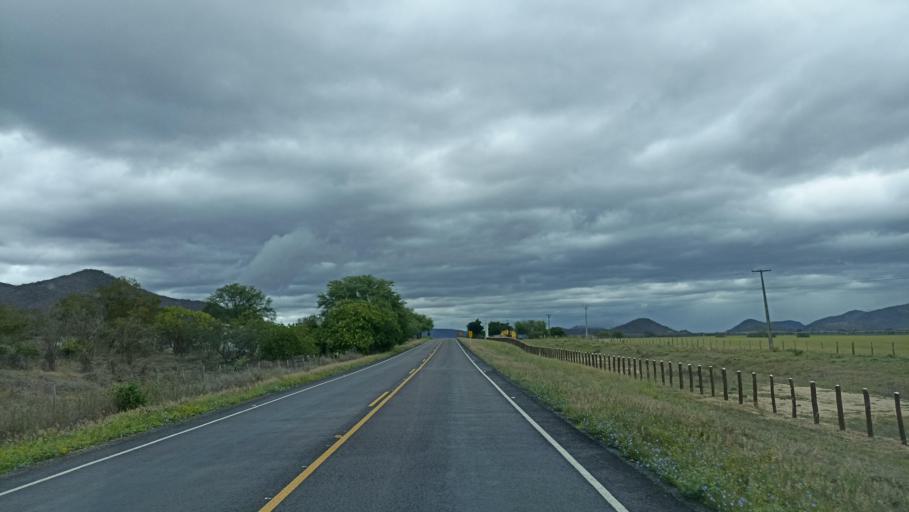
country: BR
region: Bahia
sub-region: Iacu
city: Iacu
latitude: -12.8887
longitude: -40.3951
